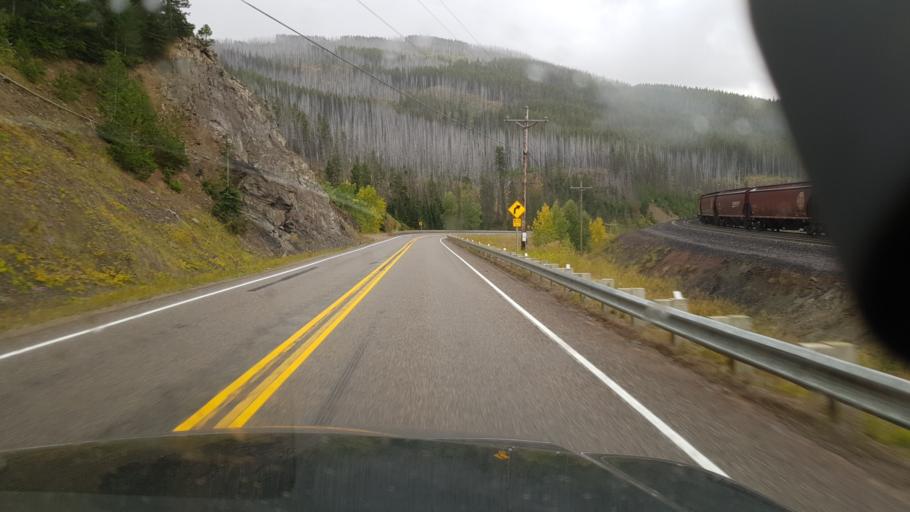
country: US
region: Montana
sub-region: Glacier County
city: South Browning
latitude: 48.3053
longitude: -113.3639
